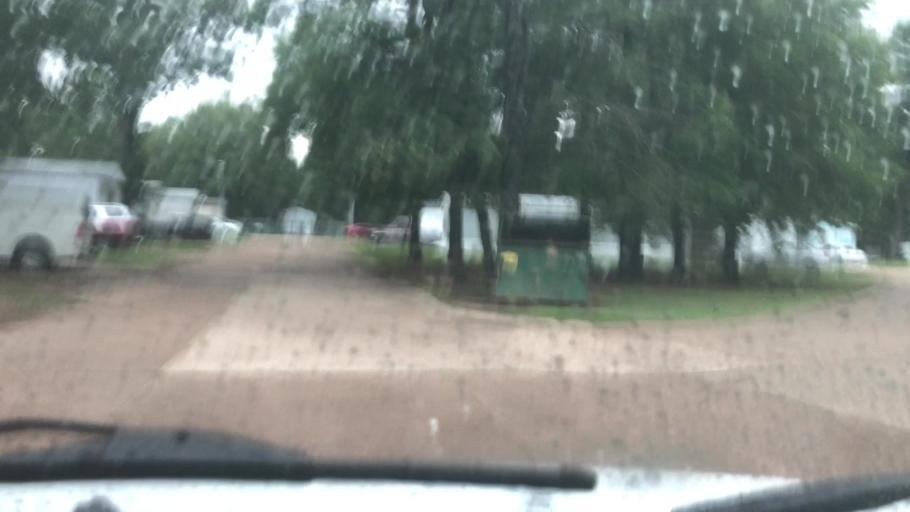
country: US
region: Texas
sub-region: Bowie County
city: Wake Village
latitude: 33.3879
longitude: -94.0784
